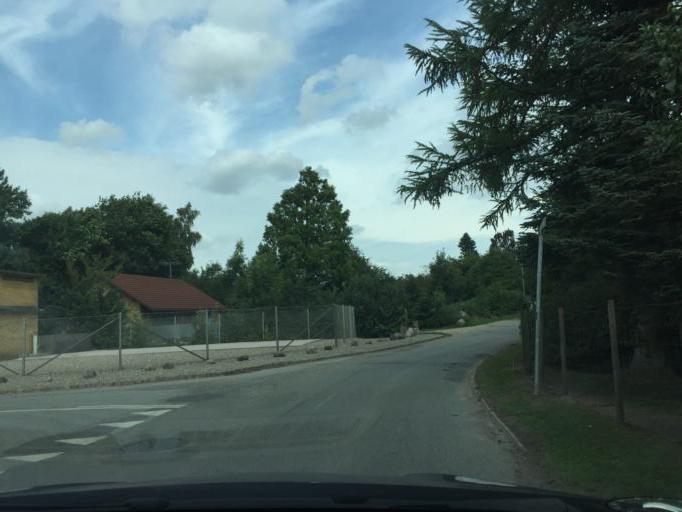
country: DK
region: South Denmark
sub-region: Assens Kommune
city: Vissenbjerg
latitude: 55.3672
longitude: 10.1519
